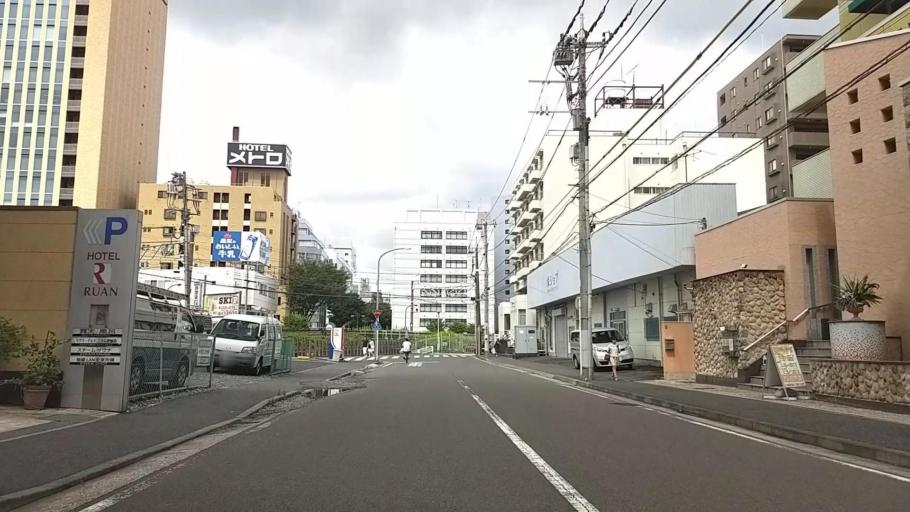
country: JP
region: Kanagawa
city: Yokohama
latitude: 35.5056
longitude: 139.6115
